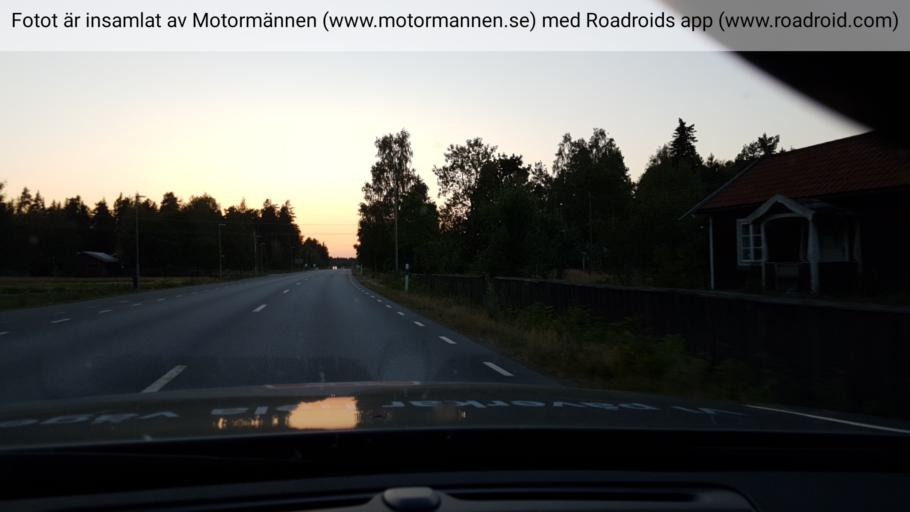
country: SE
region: Uppsala
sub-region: Heby Kommun
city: OEstervala
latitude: 60.1666
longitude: 17.1927
